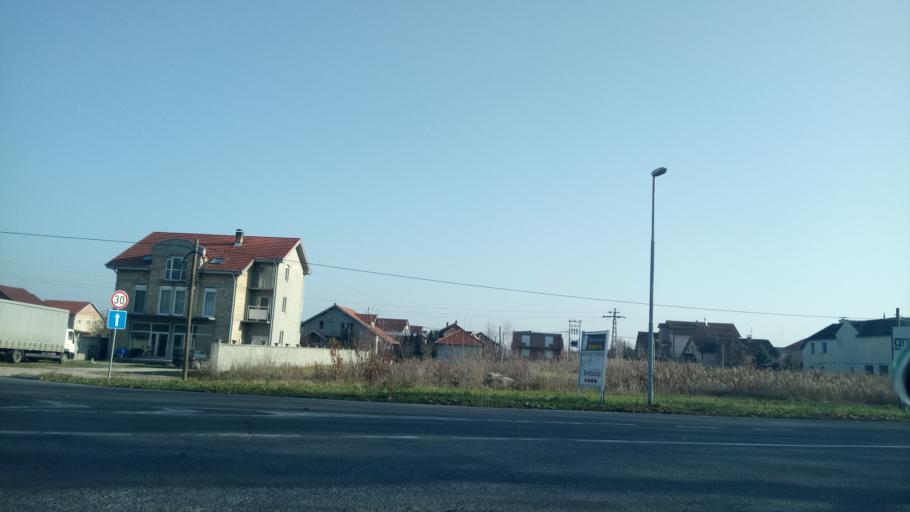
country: RS
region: Autonomna Pokrajina Vojvodina
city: Nova Pazova
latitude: 44.9527
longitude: 20.2066
